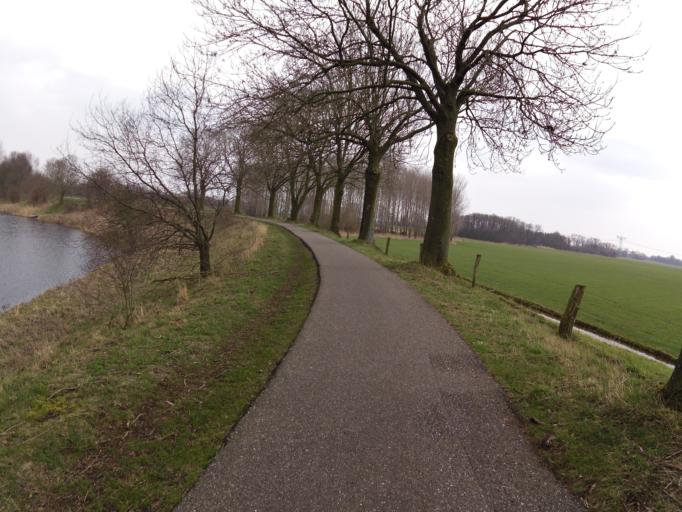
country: NL
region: North Brabant
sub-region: Gemeente Heusden
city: Heusden
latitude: 51.7072
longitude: 5.1115
